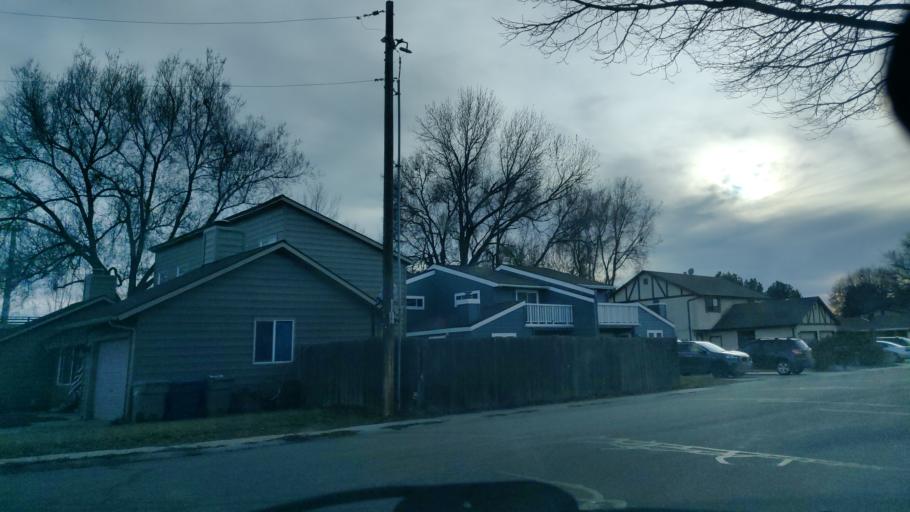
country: US
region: Idaho
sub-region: Ada County
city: Garden City
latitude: 43.6130
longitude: -116.2663
